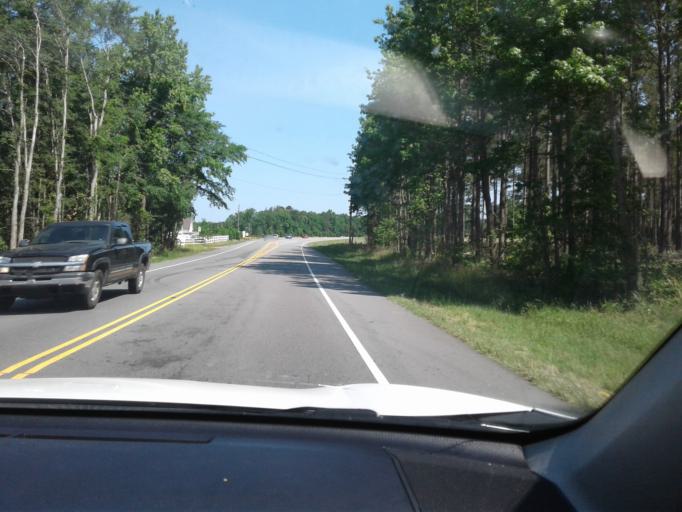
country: US
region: North Carolina
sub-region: Harnett County
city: Lillington
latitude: 35.4329
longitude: -78.8274
